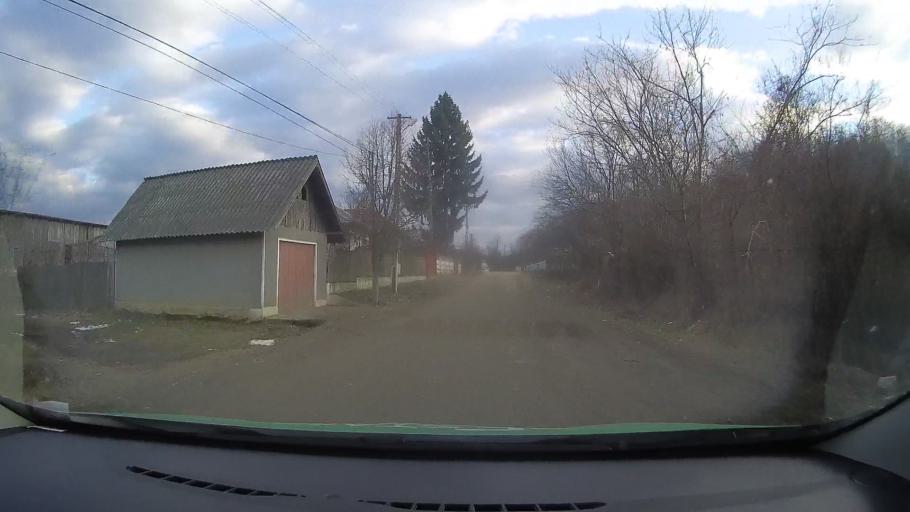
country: RO
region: Dambovita
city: Ion Luca Caragiale
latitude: 44.9124
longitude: 25.6934
